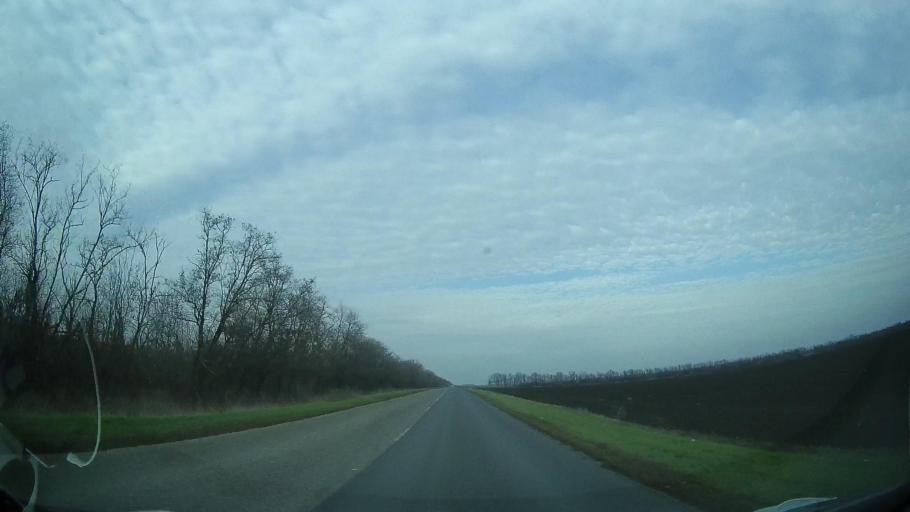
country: RU
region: Rostov
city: Zernograd
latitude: 46.9360
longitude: 40.3665
